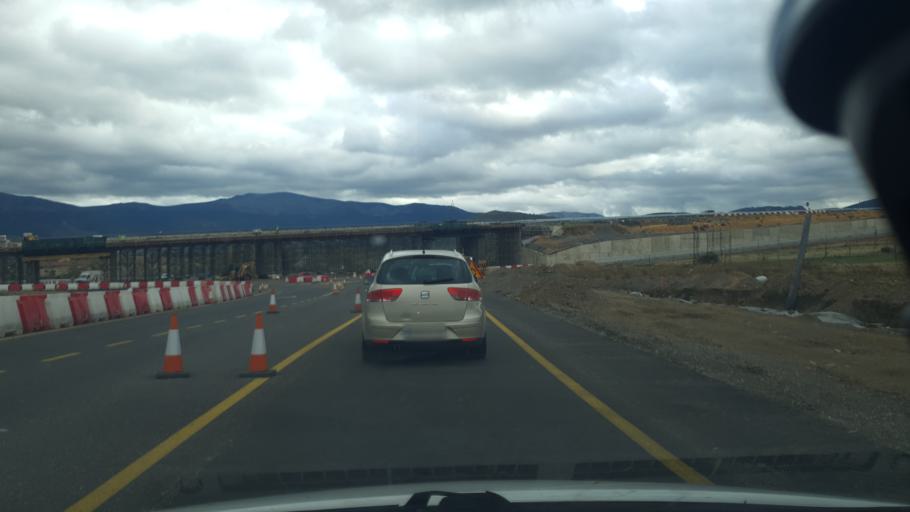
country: ES
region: Castille and Leon
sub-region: Provincia de Segovia
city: San Cristobal de Segovia
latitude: 40.9284
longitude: -4.0883
